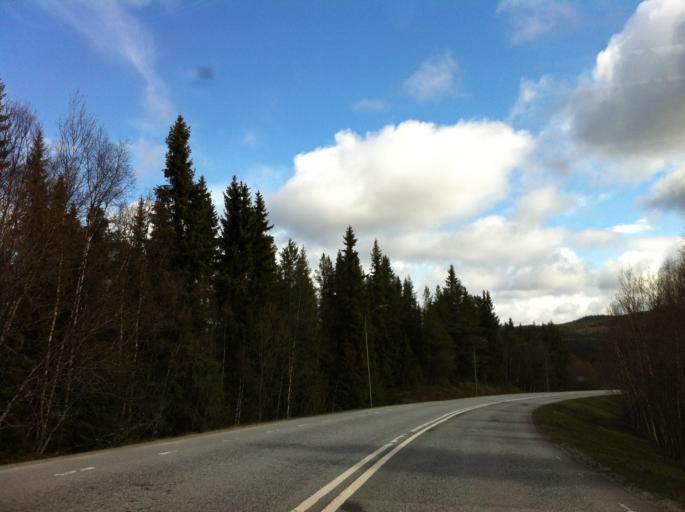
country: NO
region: Hedmark
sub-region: Engerdal
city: Engerdal
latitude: 62.5447
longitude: 12.4691
